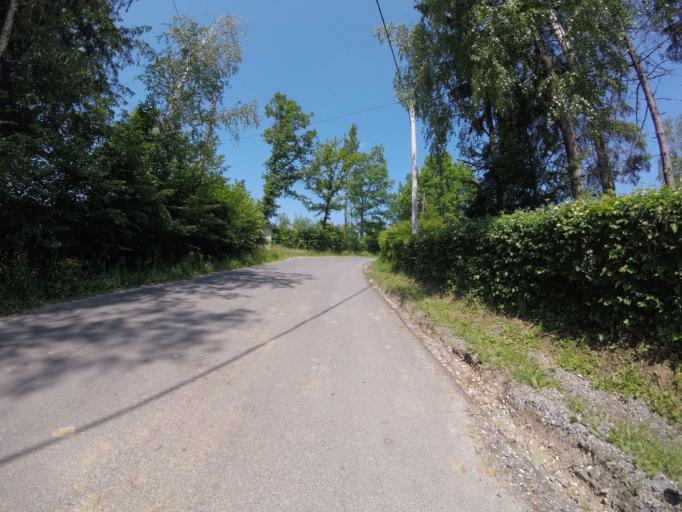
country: HR
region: Grad Zagreb
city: Strmec
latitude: 45.5704
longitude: 15.9470
